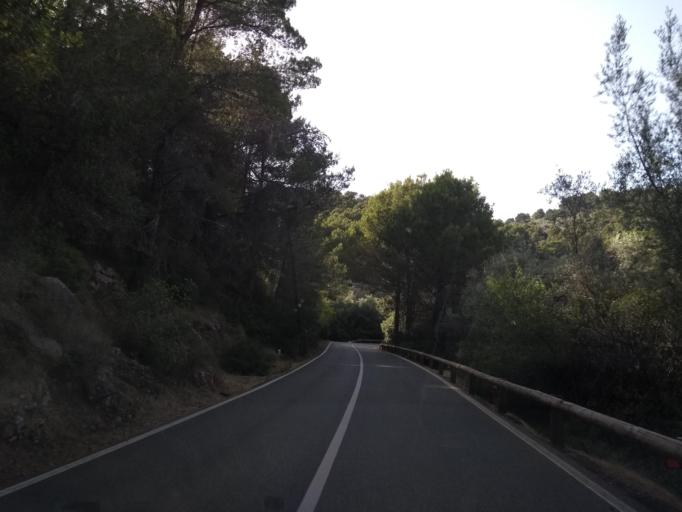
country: ES
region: Balearic Islands
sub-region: Illes Balears
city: Fornalutx
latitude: 39.7825
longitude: 2.7310
